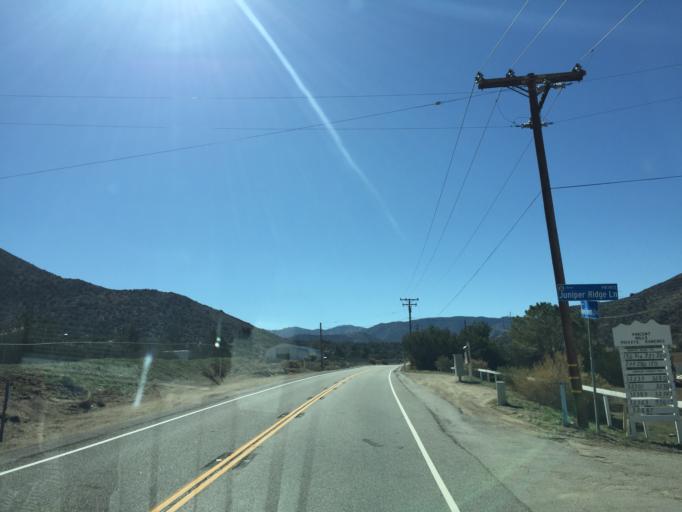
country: US
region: California
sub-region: Los Angeles County
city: Vincent
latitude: 34.4736
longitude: -118.1157
